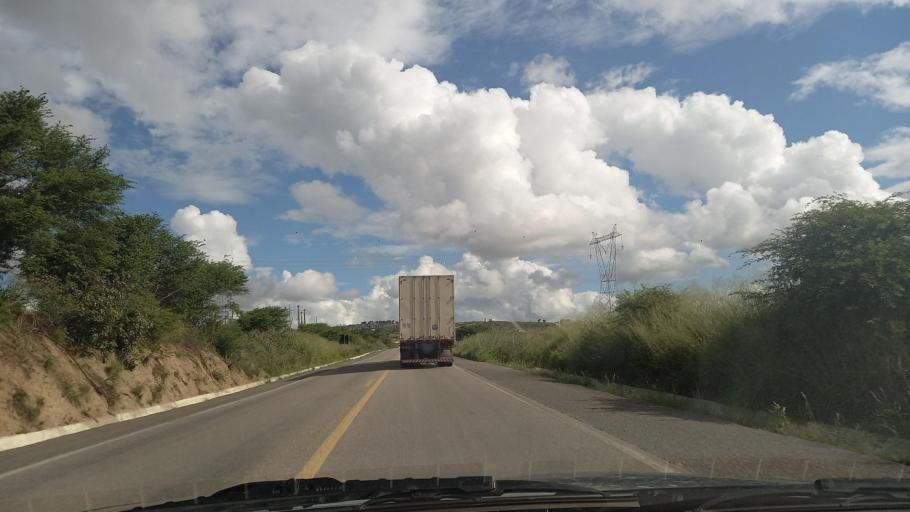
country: BR
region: Pernambuco
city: Garanhuns
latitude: -8.8482
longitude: -36.4606
